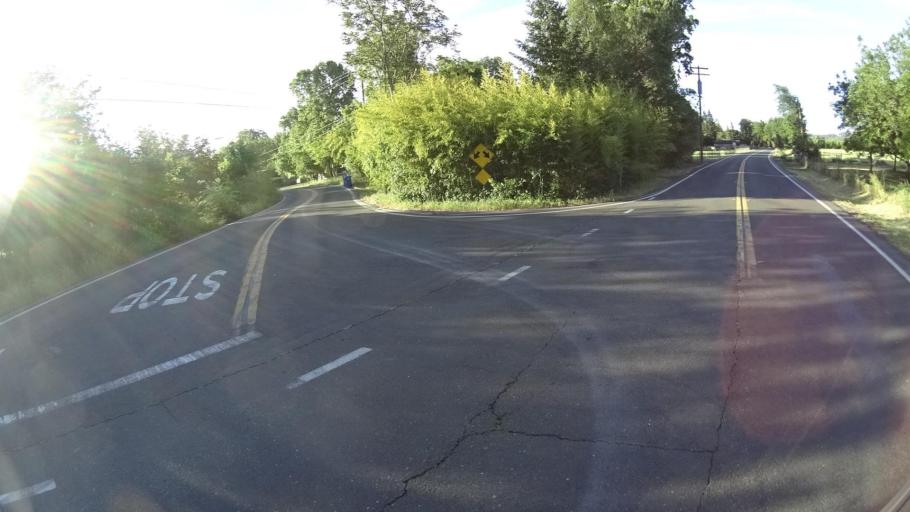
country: US
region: California
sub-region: Lake County
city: Upper Lake
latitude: 39.1683
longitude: -122.9117
